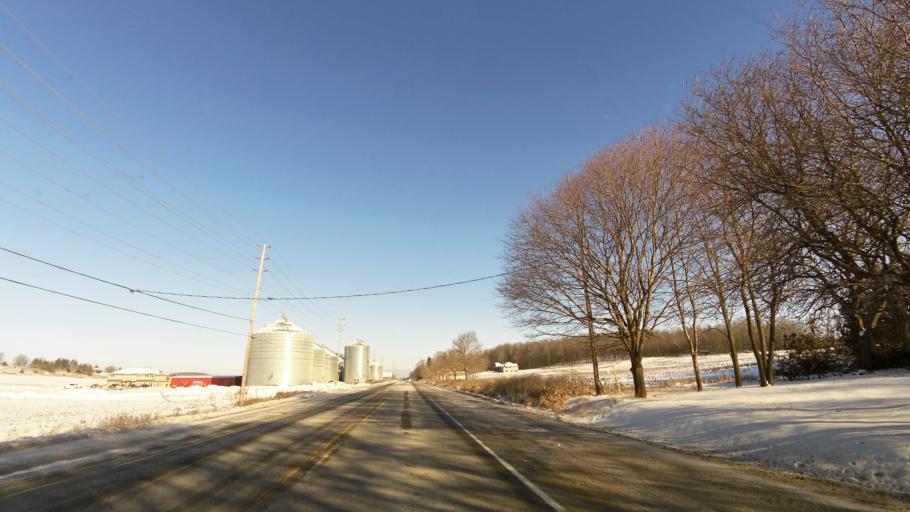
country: CA
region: Ontario
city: Quinte West
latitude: 44.2190
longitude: -77.8275
